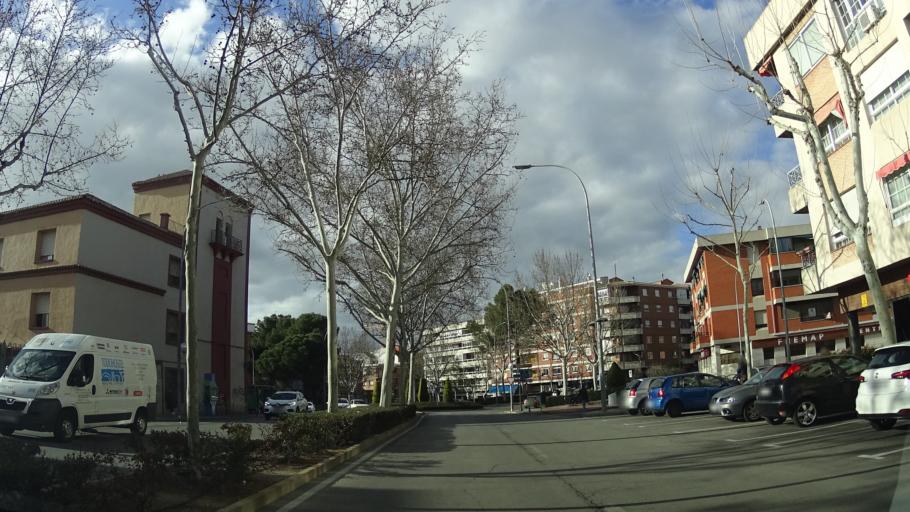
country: ES
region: Castille-La Mancha
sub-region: Provincia de Ciudad Real
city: Ciudad Real
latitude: 38.9822
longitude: -3.9254
